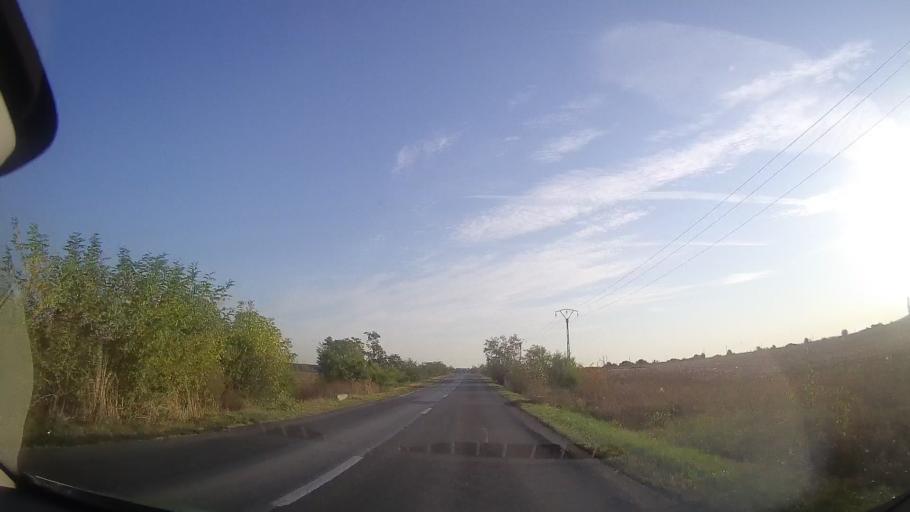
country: RO
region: Timis
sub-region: Comuna Pischia
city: Pischia
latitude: 45.8867
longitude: 21.3464
